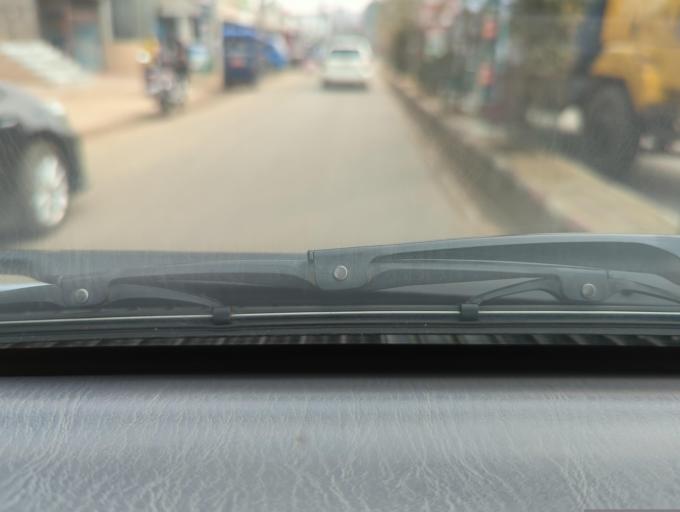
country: BD
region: Sylhet
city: Maulavi Bazar
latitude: 24.4878
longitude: 91.7640
